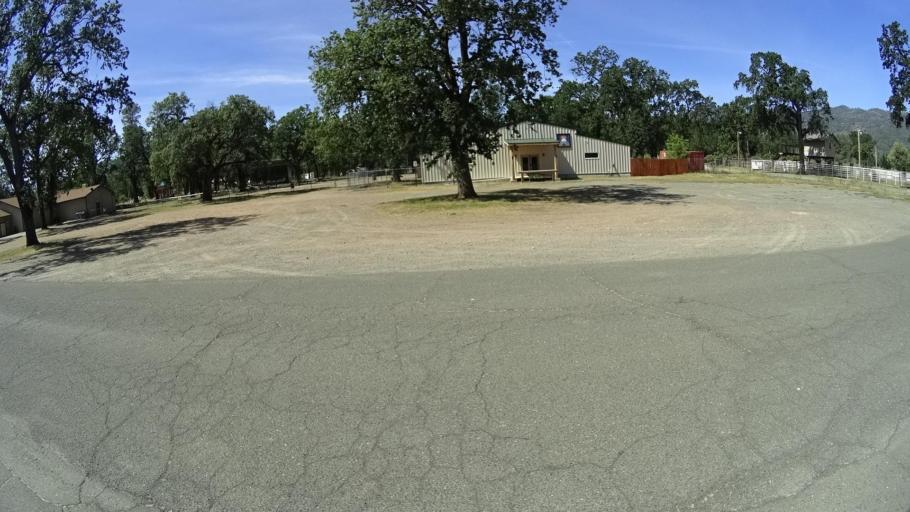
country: US
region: California
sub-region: Lake County
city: Middletown
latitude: 38.7462
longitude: -122.6241
